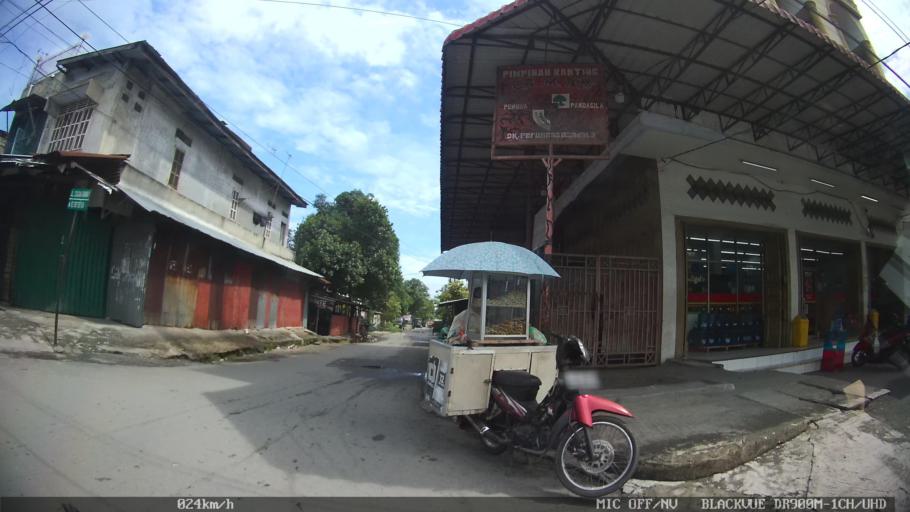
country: ID
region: North Sumatra
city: Medan
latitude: 3.5871
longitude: 98.7211
